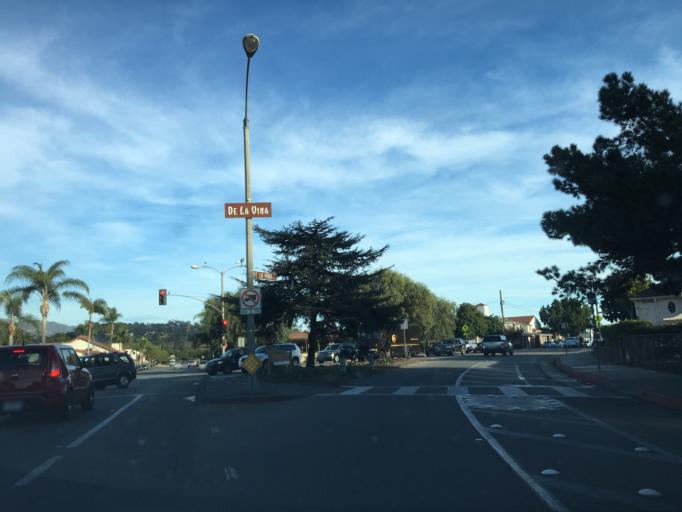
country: US
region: California
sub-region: Santa Barbara County
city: Mission Canyon
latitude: 34.4403
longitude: -119.7305
